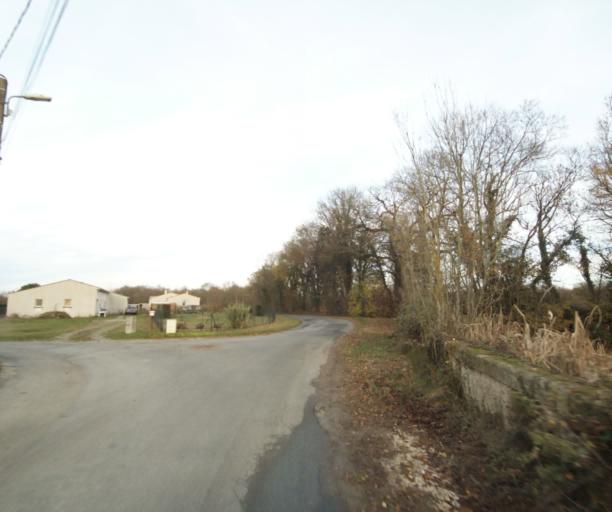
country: FR
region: Poitou-Charentes
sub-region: Departement de la Charente-Maritime
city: Fontcouverte
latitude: 45.7960
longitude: -0.5895
